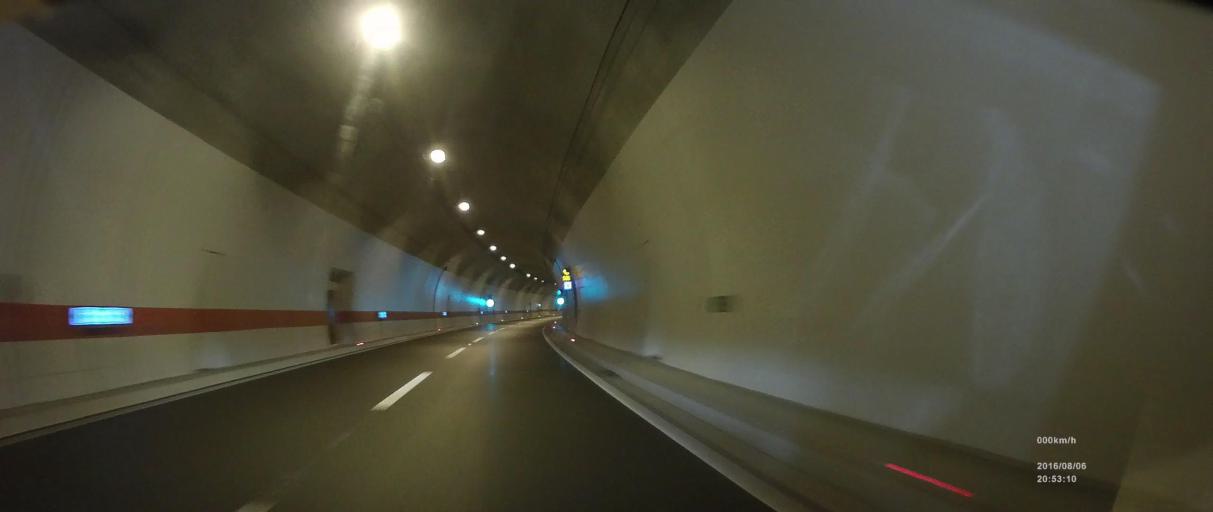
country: BA
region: Federation of Bosnia and Herzegovina
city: Ljubuski
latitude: 43.1397
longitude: 17.4845
